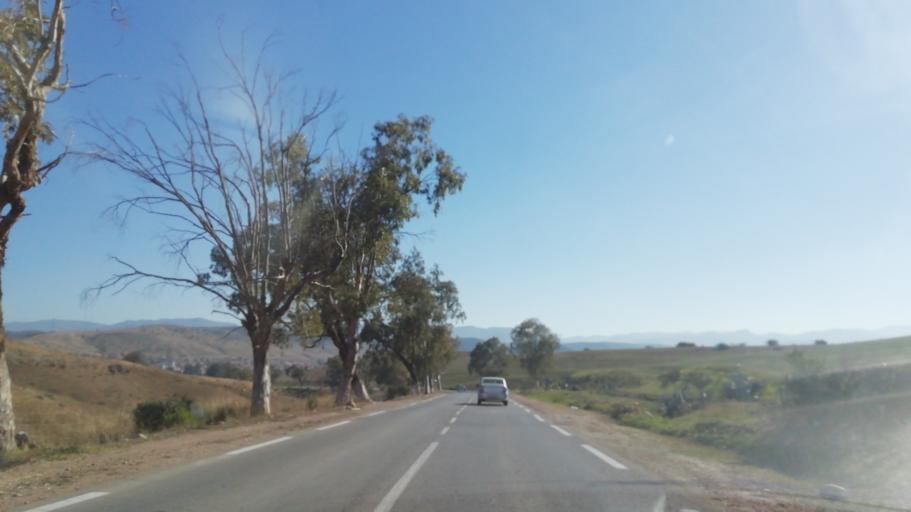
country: DZ
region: Tlemcen
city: Nedroma
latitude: 34.8297
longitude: -1.6648
